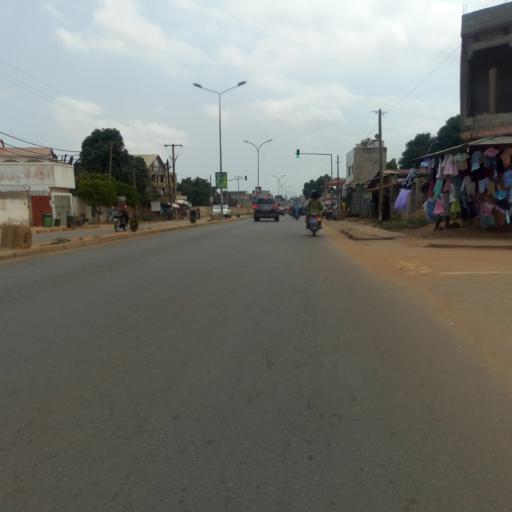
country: TG
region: Maritime
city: Lome
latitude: 6.1956
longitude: 1.1761
